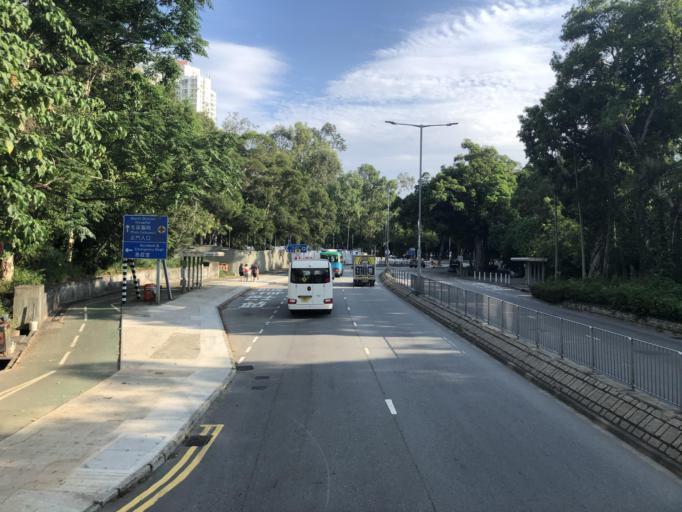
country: HK
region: Tai Po
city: Tai Po
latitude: 22.4982
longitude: 114.1230
